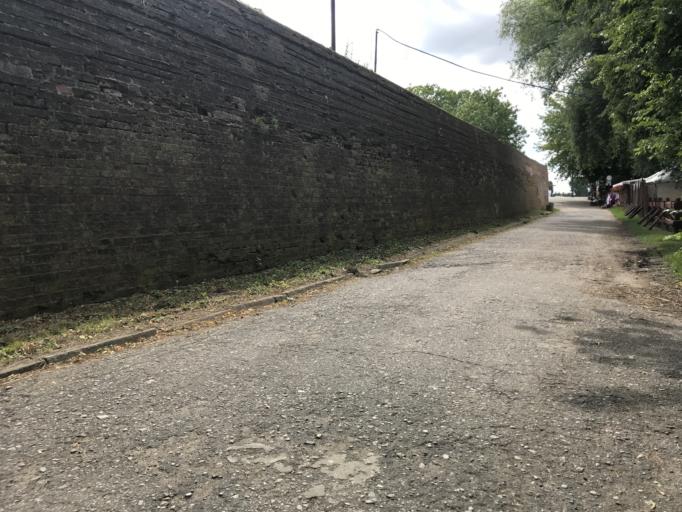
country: PL
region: Pomeranian Voivodeship
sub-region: Powiat malborski
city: Malbork
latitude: 54.0418
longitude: 19.0286
